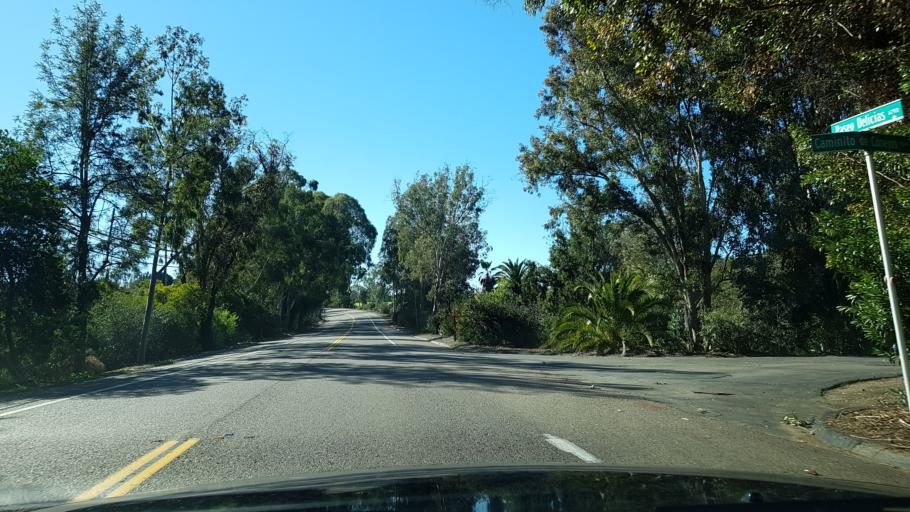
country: US
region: California
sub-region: San Diego County
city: Rancho Santa Fe
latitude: 33.0337
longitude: -117.1875
